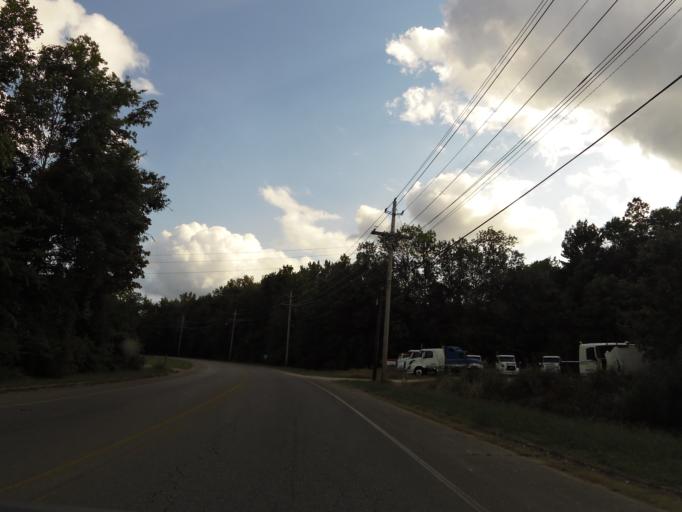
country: US
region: Mississippi
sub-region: Alcorn County
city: Corinth
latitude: 34.9337
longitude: -88.5273
